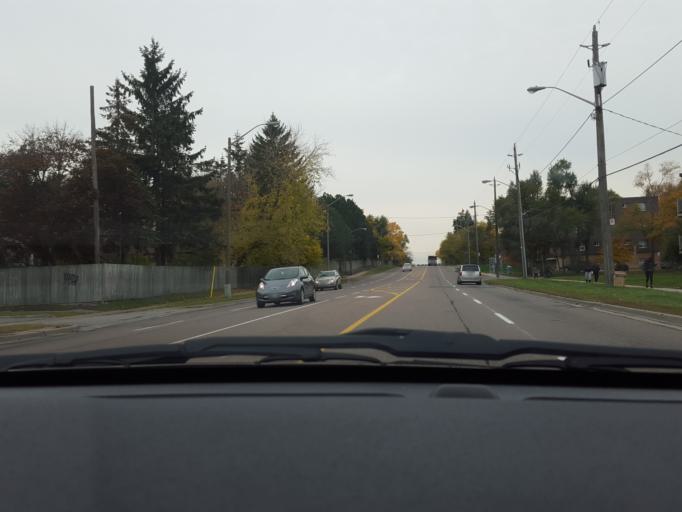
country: CA
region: Ontario
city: Willowdale
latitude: 43.7360
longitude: -79.3490
